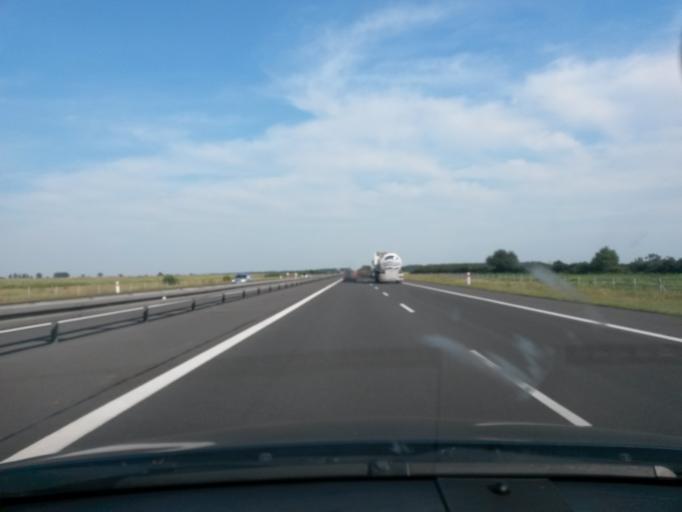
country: PL
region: Greater Poland Voivodeship
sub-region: Powiat wrzesinski
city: Wrzesnia
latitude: 52.3004
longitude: 17.6265
